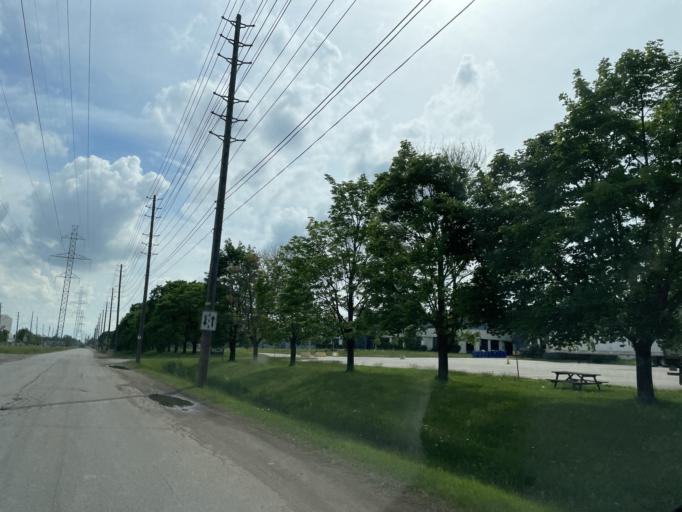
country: CA
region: Ontario
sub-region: Wellington County
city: Guelph
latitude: 43.5516
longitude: -80.2876
